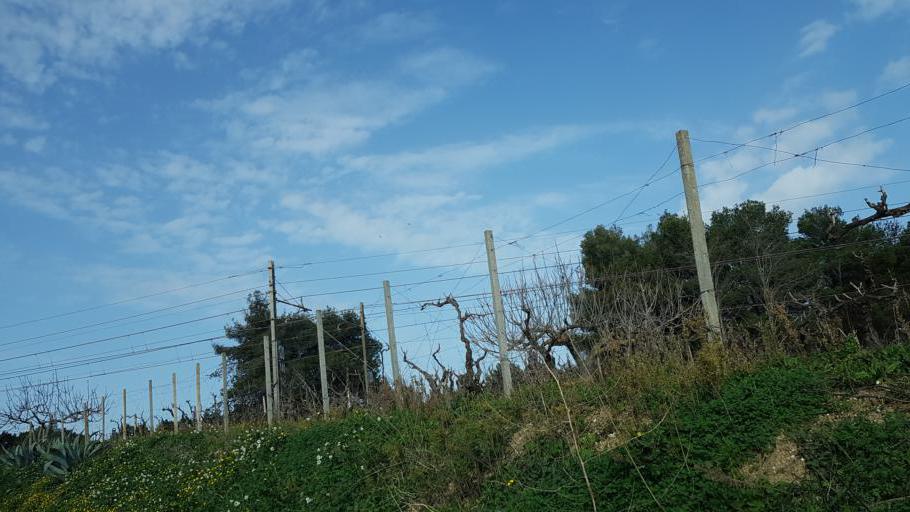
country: IT
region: Apulia
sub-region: Provincia di Brindisi
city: Brindisi
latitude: 40.6233
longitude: 17.9052
